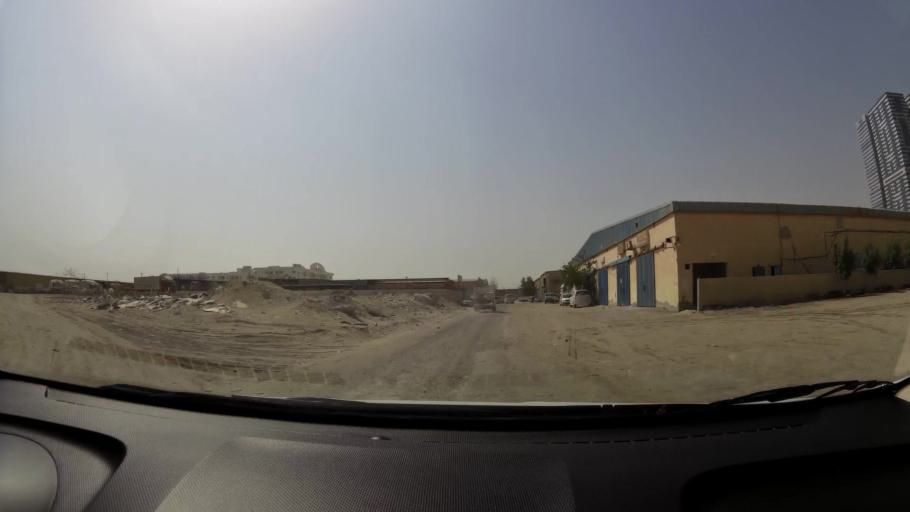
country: AE
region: Ash Shariqah
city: Sharjah
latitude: 25.3064
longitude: 55.3848
